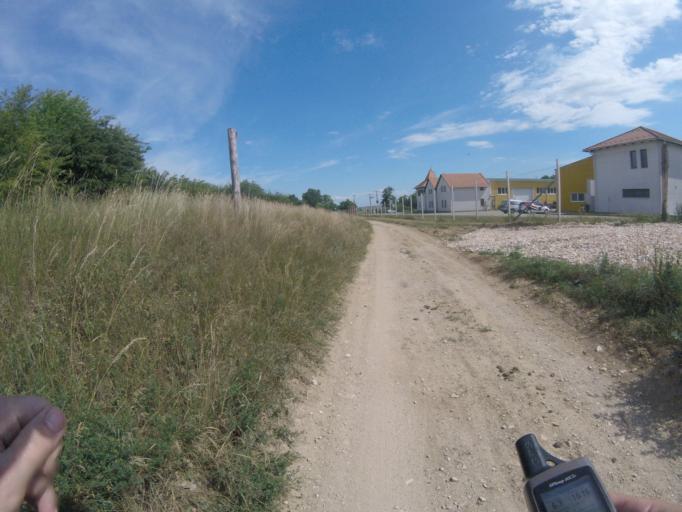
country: HU
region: Fejer
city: Szarliget
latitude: 47.4846
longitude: 18.5022
